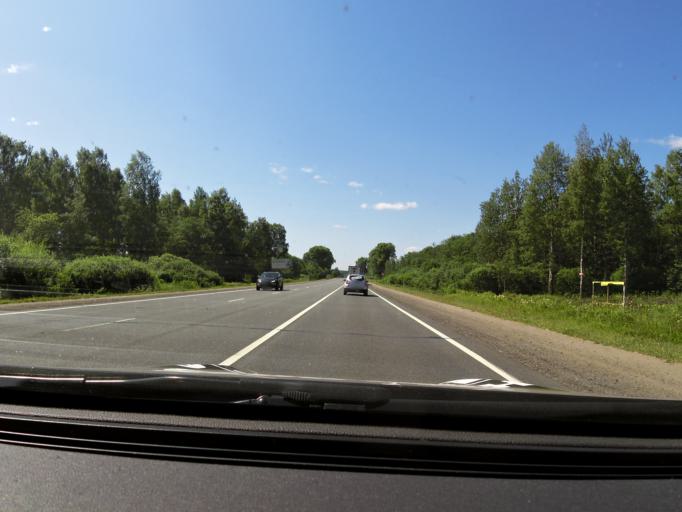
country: RU
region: Novgorod
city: Valday
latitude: 58.0289
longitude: 32.9962
